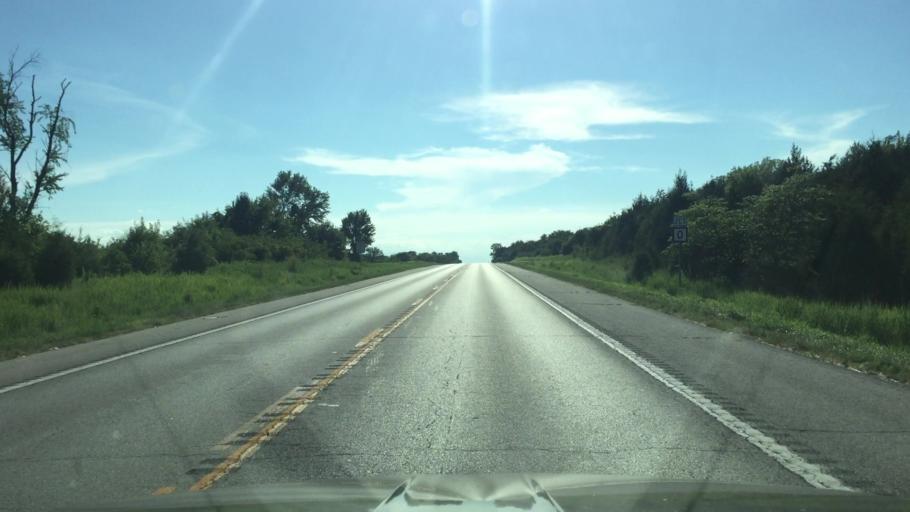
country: US
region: Missouri
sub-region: Pettis County
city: Sedalia
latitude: 38.6947
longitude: -93.1223
